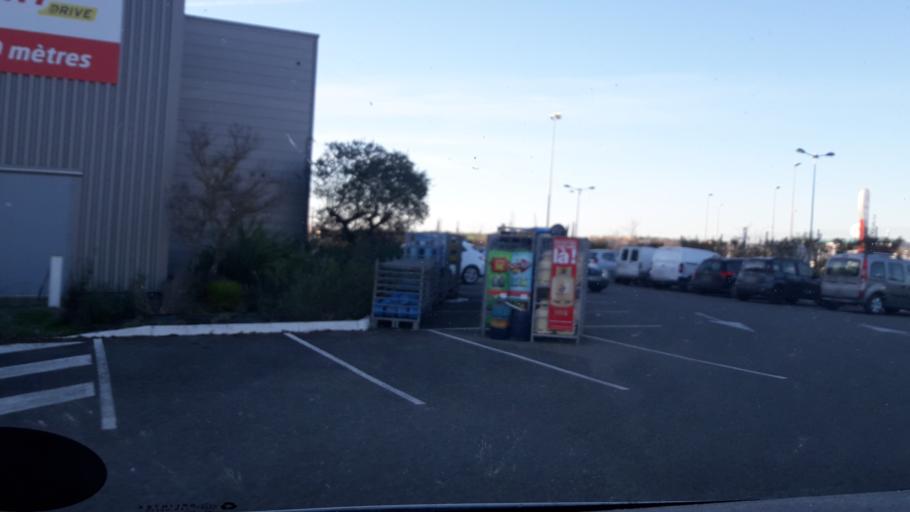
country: FR
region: Midi-Pyrenees
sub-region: Departement du Gers
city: Pujaudran
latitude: 43.6003
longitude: 1.0688
